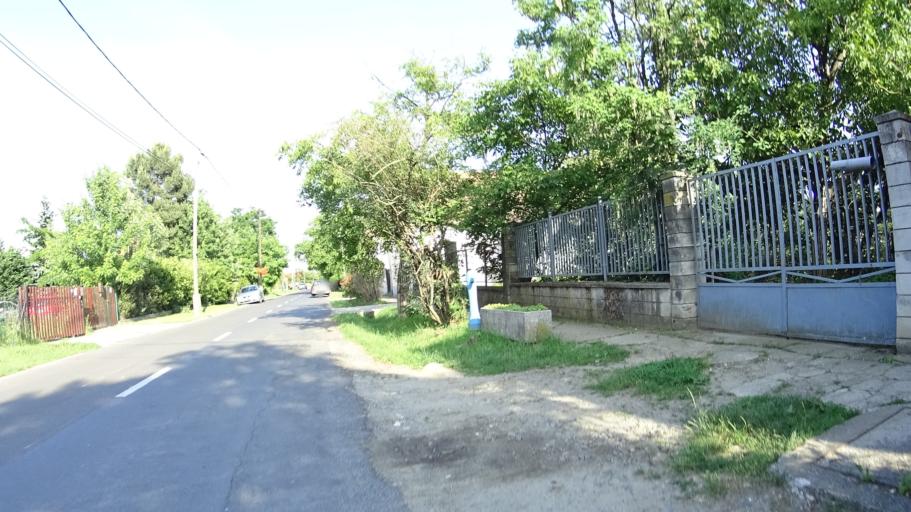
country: HU
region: Pest
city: Veroce
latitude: 47.8060
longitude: 19.0155
